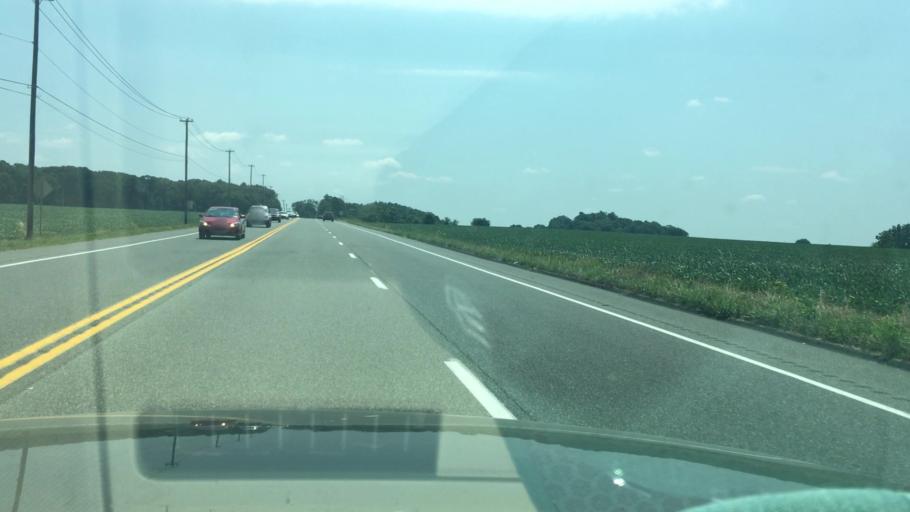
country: US
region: Pennsylvania
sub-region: Lehigh County
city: Schnecksville
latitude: 40.6207
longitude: -75.6627
